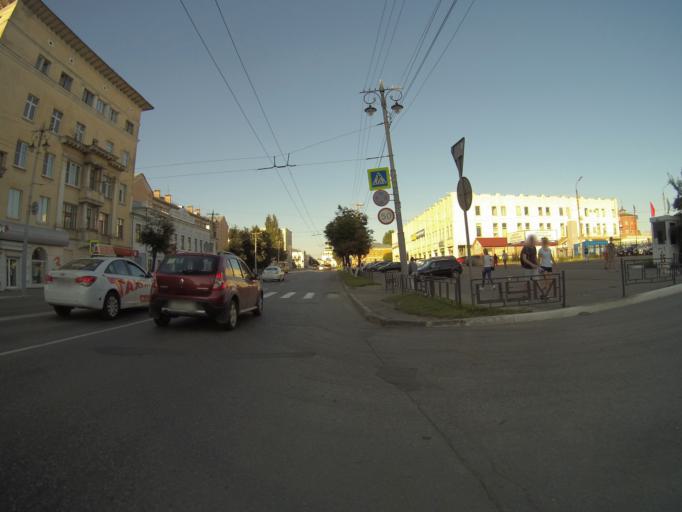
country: RU
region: Vladimir
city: Vladimir
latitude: 56.1259
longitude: 40.3906
